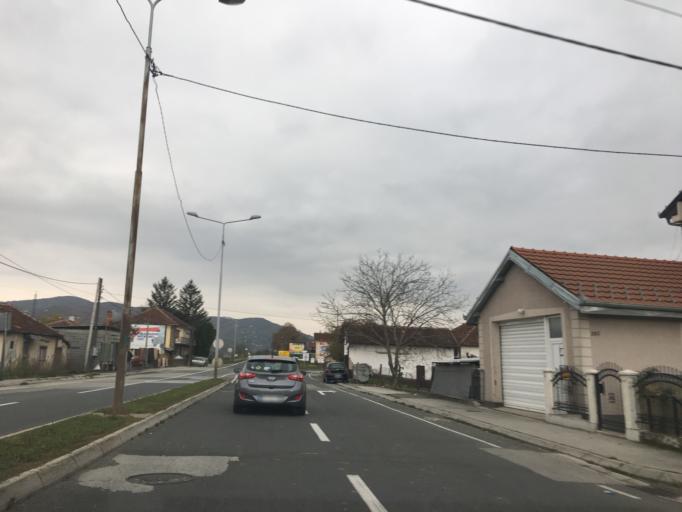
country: RS
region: Central Serbia
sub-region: Raski Okrug
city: Kraljevo
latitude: 43.7266
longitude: 20.7228
